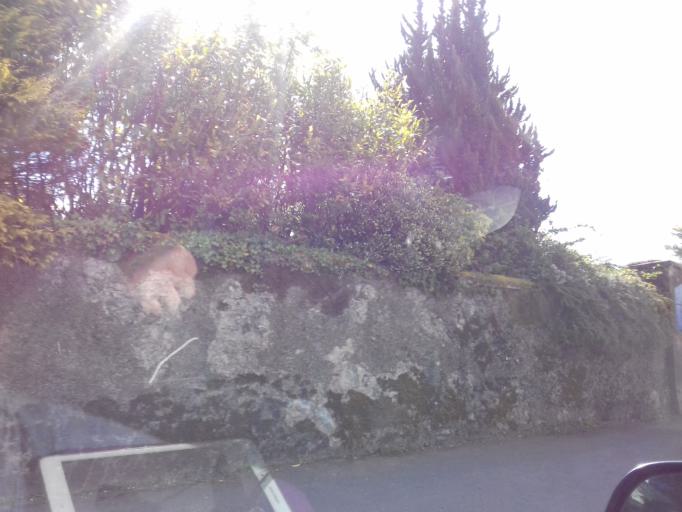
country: IE
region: Leinster
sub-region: Loch Garman
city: Castlebridge
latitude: 52.3823
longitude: -6.4502
